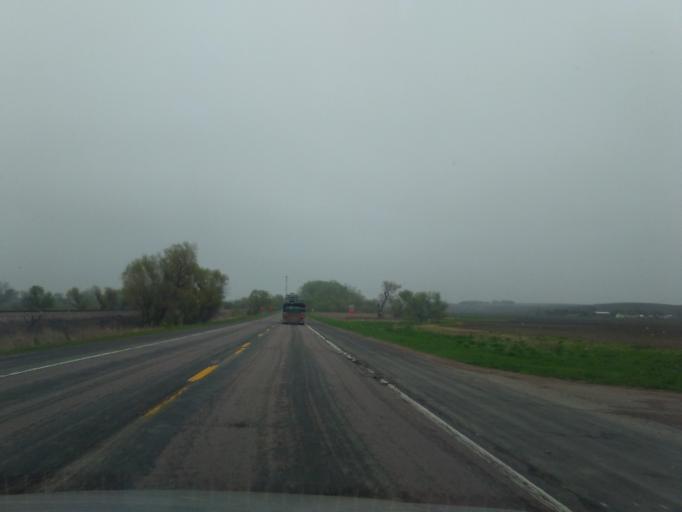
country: US
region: Nebraska
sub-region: Burt County
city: Oakland
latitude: 41.8034
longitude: -96.4805
